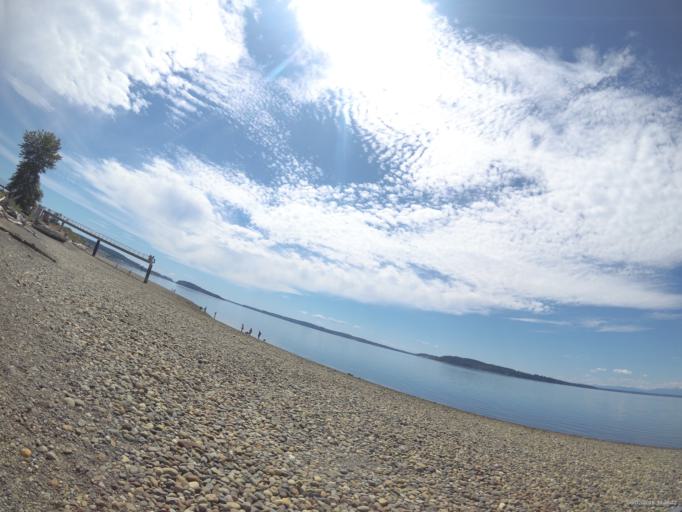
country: US
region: Washington
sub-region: Pierce County
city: Steilacoom
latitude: 47.2017
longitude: -122.5826
